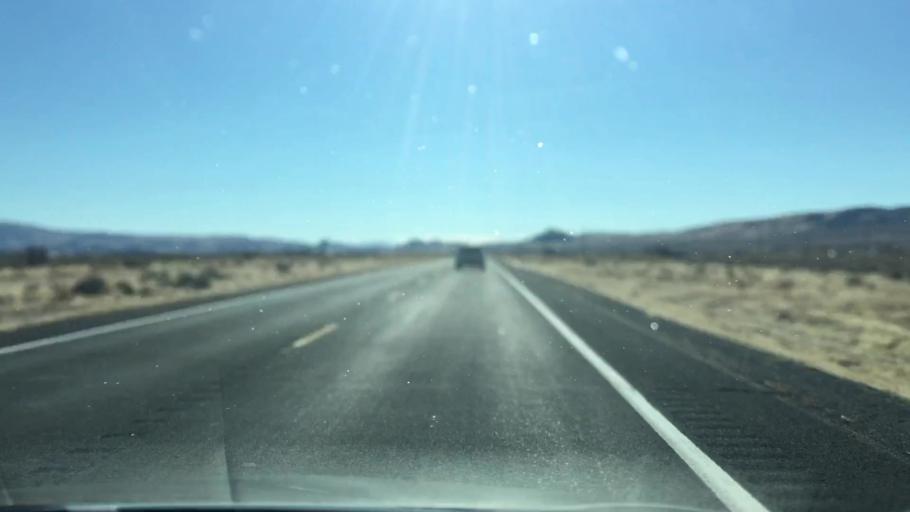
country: US
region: Nevada
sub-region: Lyon County
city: Silver Springs
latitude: 39.3862
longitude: -119.2321
